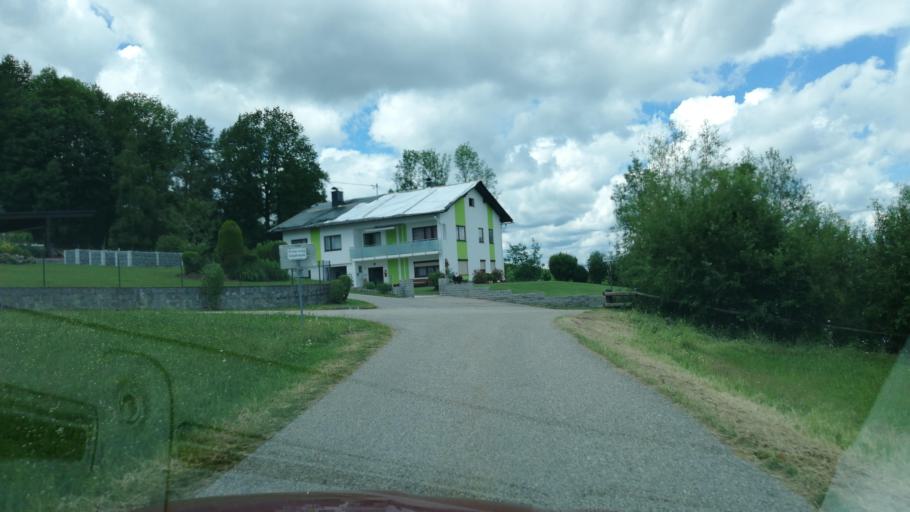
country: AT
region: Upper Austria
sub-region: Politischer Bezirk Urfahr-Umgebung
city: Haibach im Muhlkreis
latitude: 48.4430
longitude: 14.3471
